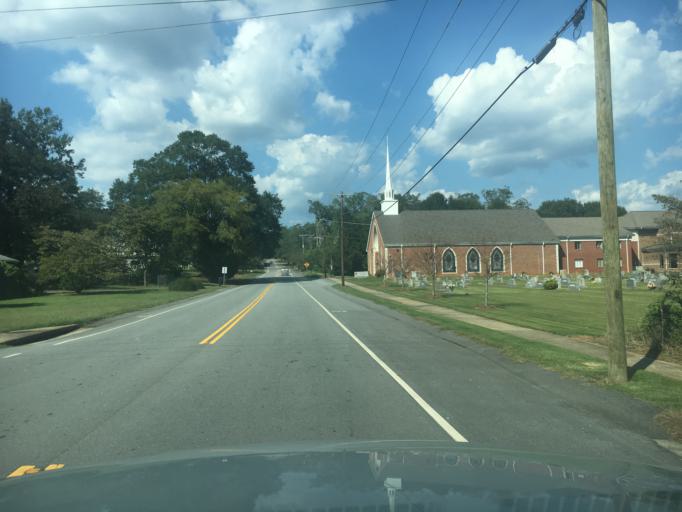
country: US
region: South Carolina
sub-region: Anderson County
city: Pendleton
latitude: 34.6480
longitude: -82.7822
